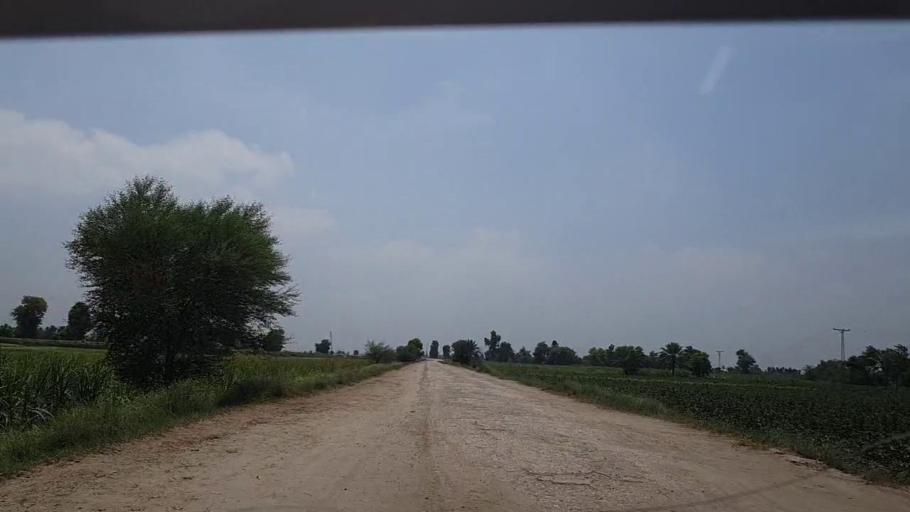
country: PK
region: Sindh
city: Khanpur
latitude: 27.9112
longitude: 69.3942
